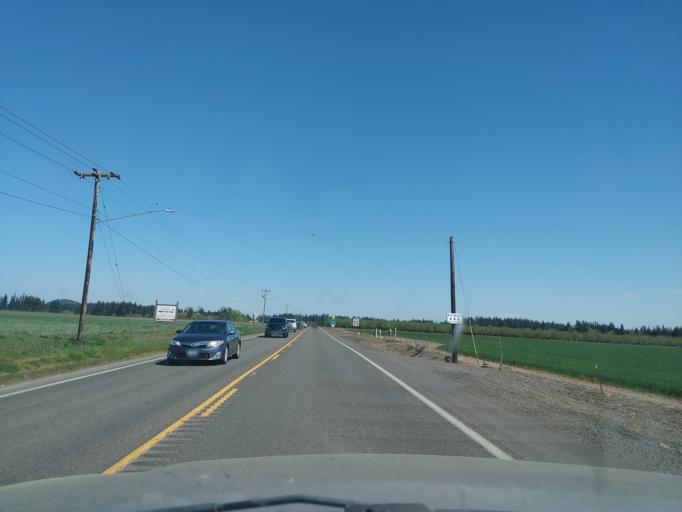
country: US
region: Oregon
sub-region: Yamhill County
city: Newberg
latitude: 45.2342
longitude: -122.9098
